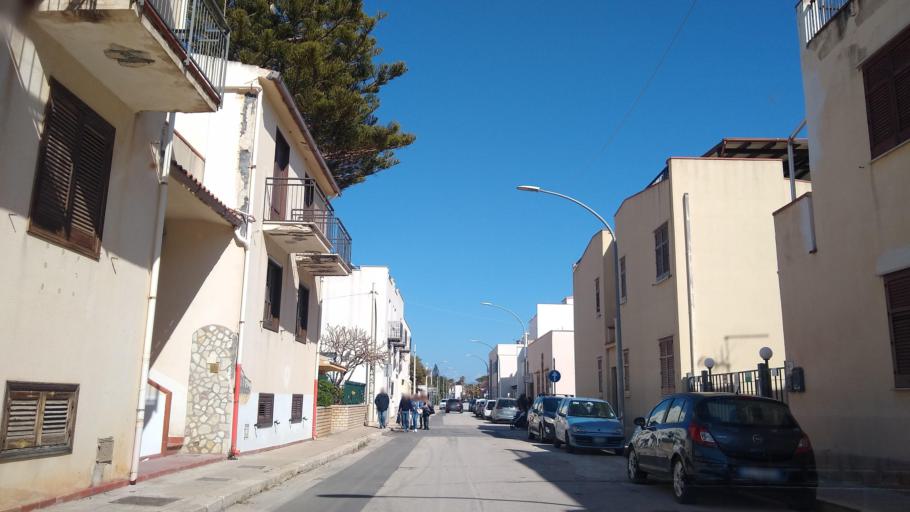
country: IT
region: Sicily
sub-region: Trapani
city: San Vito Lo Capo
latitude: 38.1750
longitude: 12.7378
